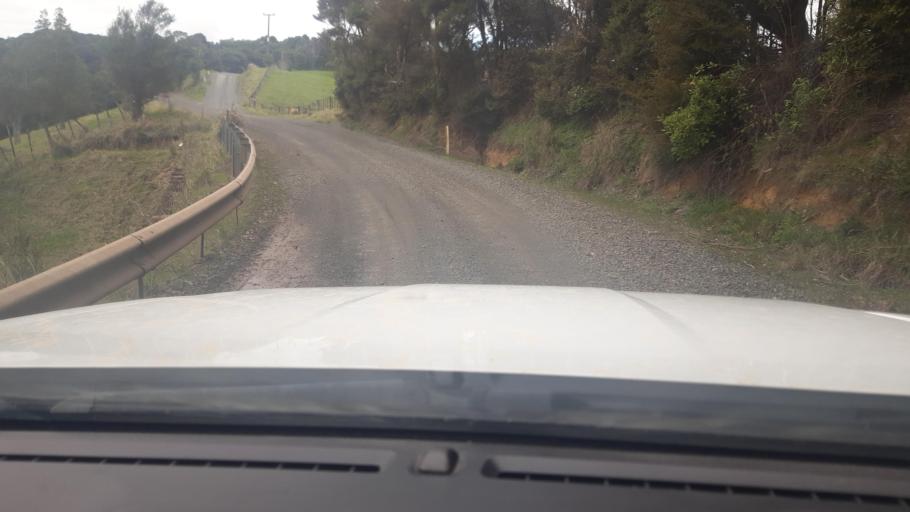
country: NZ
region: Northland
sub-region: Far North District
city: Kaitaia
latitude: -35.0717
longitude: 173.3307
